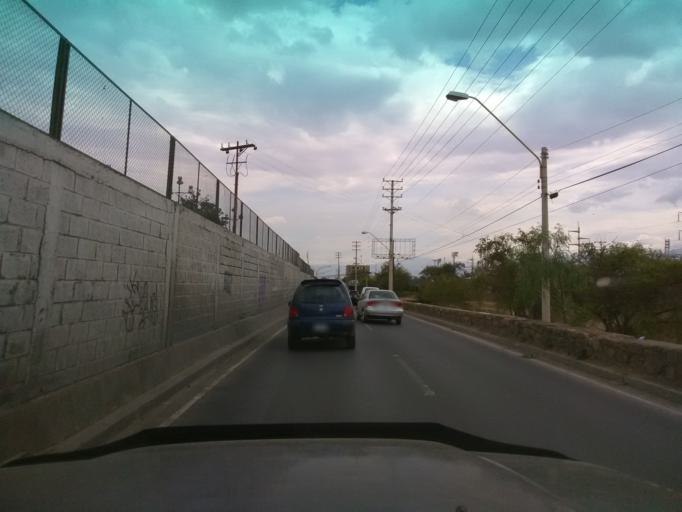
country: BO
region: Cochabamba
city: Cochabamba
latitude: -17.3812
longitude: -66.1583
